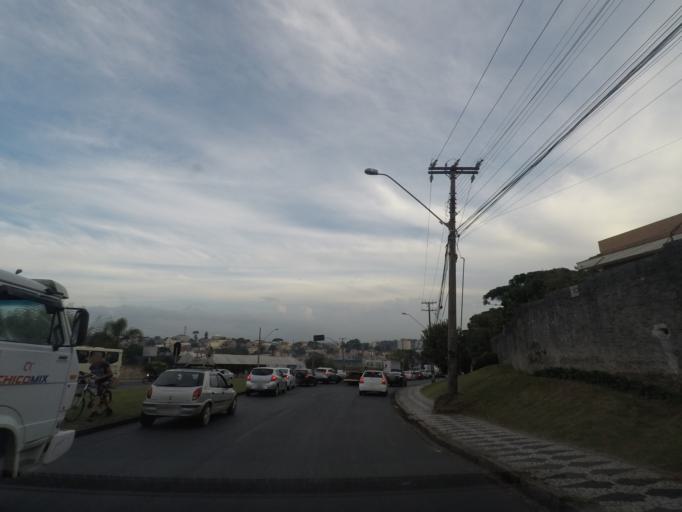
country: BR
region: Parana
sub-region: Curitiba
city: Curitiba
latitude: -25.3746
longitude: -49.2234
